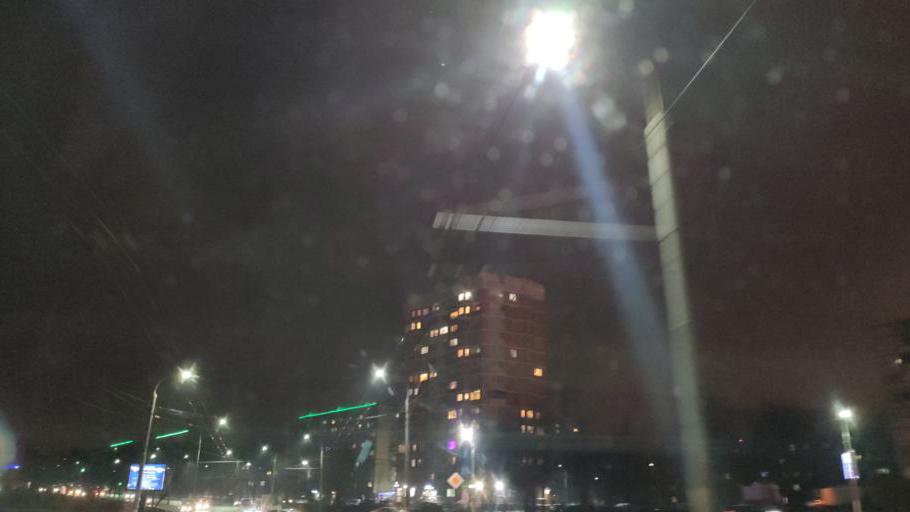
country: RU
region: Moskovskaya
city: Dubrovitsy
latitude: 55.4262
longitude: 37.5056
